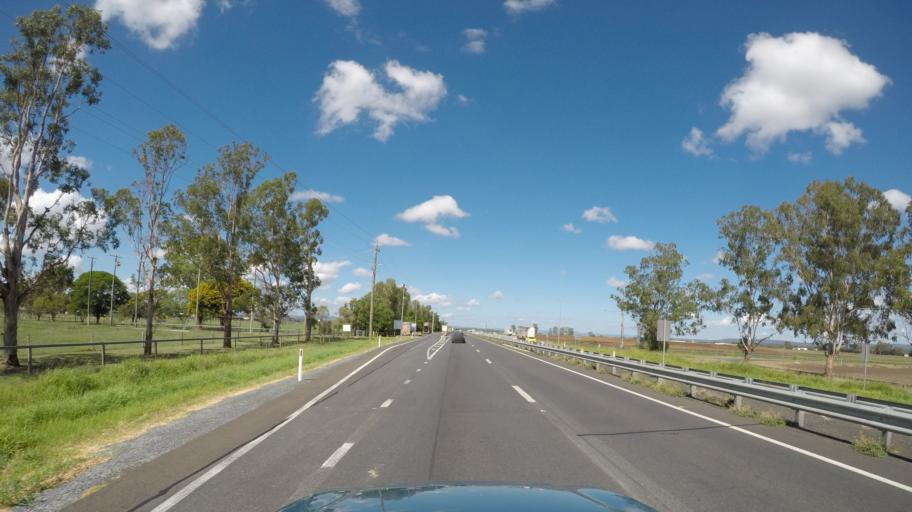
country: AU
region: Queensland
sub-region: Lockyer Valley
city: Gatton
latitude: -27.5490
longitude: 152.3324
